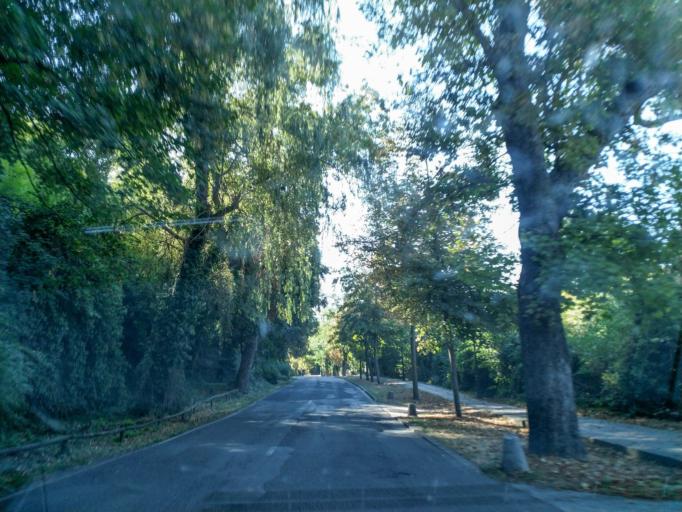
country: ES
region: Castille and Leon
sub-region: Provincia de Segovia
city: Segovia
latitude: 40.9537
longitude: -4.1251
